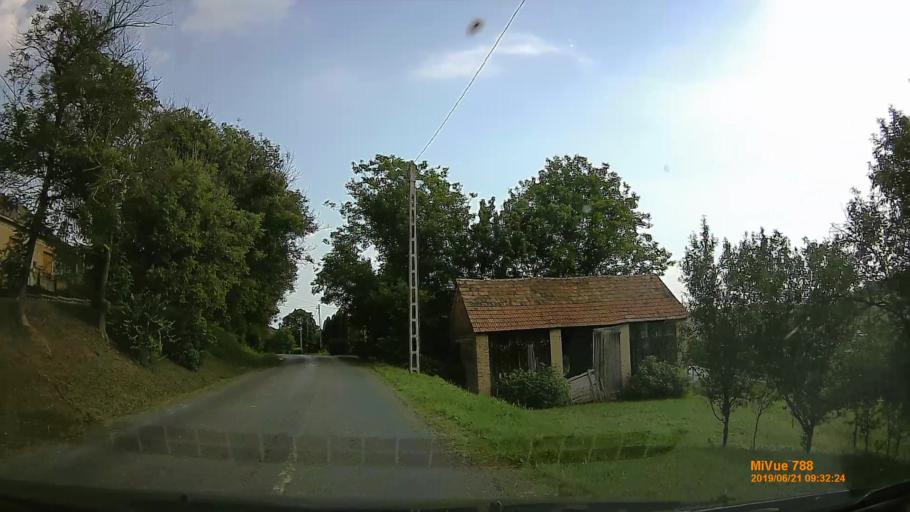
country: HU
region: Somogy
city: Taszar
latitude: 46.3118
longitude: 17.8835
